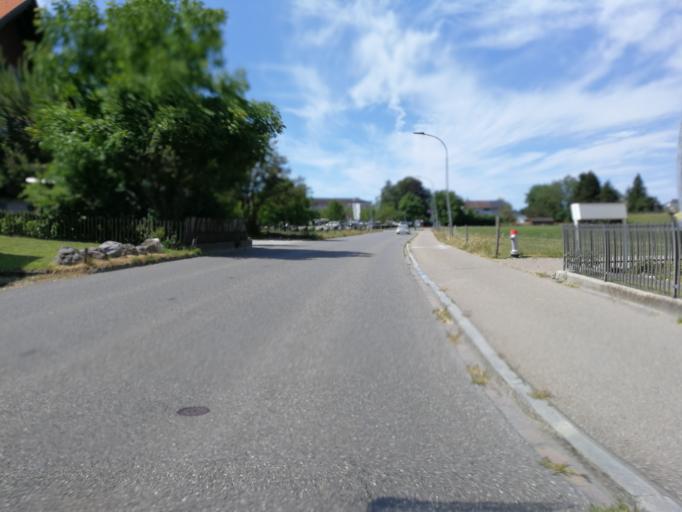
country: CH
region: Zurich
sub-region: Bezirk Hinwil
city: Wetzikon / Ober-Wetzikon
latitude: 47.3230
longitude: 8.8043
